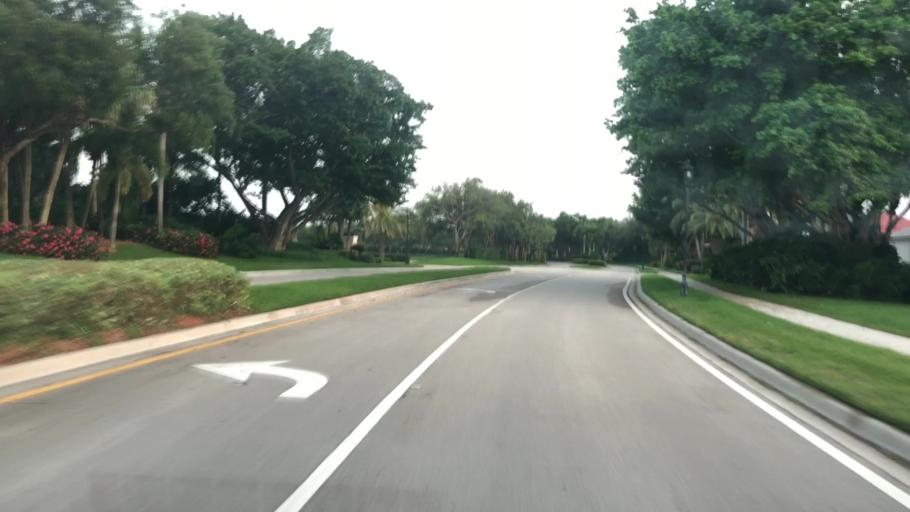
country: US
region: Florida
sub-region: Broward County
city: Weston
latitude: 26.0921
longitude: -80.4006
